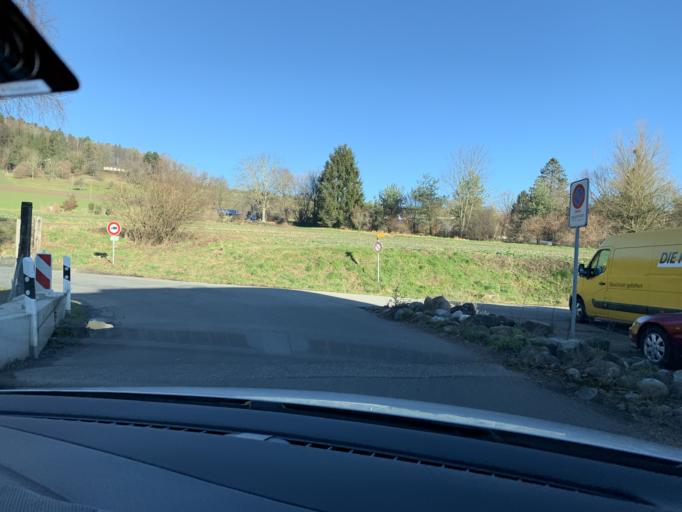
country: CH
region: Zurich
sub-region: Bezirk Dielsdorf
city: Sonnhalde
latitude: 47.4606
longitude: 8.4434
